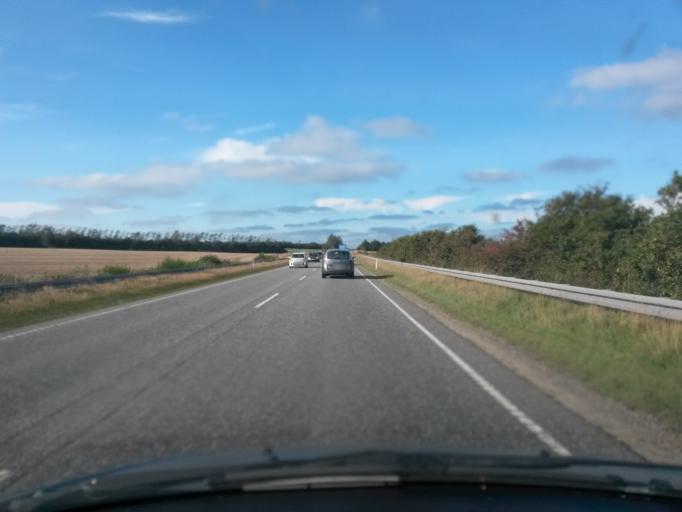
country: DK
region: Central Jutland
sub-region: Herning Kommune
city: Avlum
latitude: 56.2703
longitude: 8.7668
